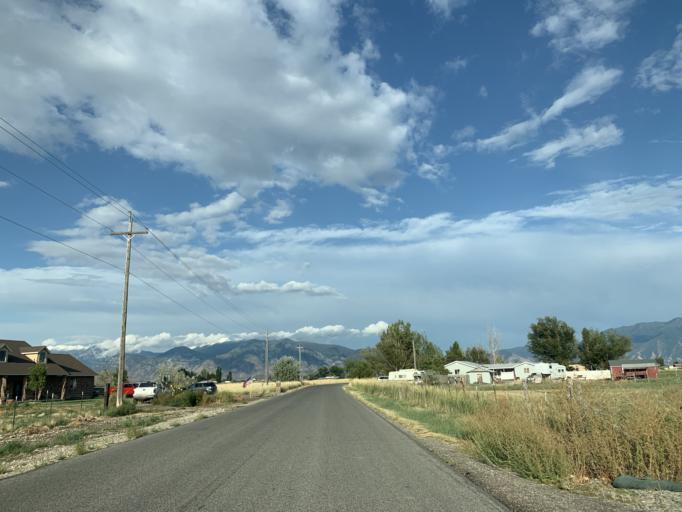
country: US
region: Utah
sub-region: Utah County
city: Benjamin
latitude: 40.1158
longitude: -111.7761
